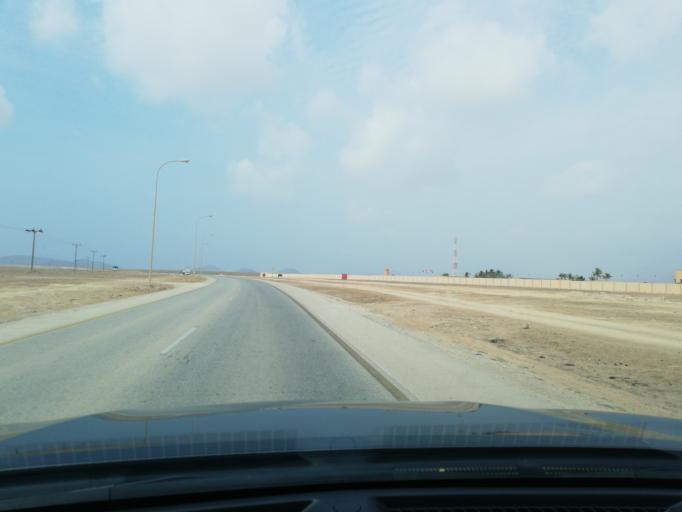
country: OM
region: Zufar
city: Salalah
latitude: 16.9414
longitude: 53.8462
